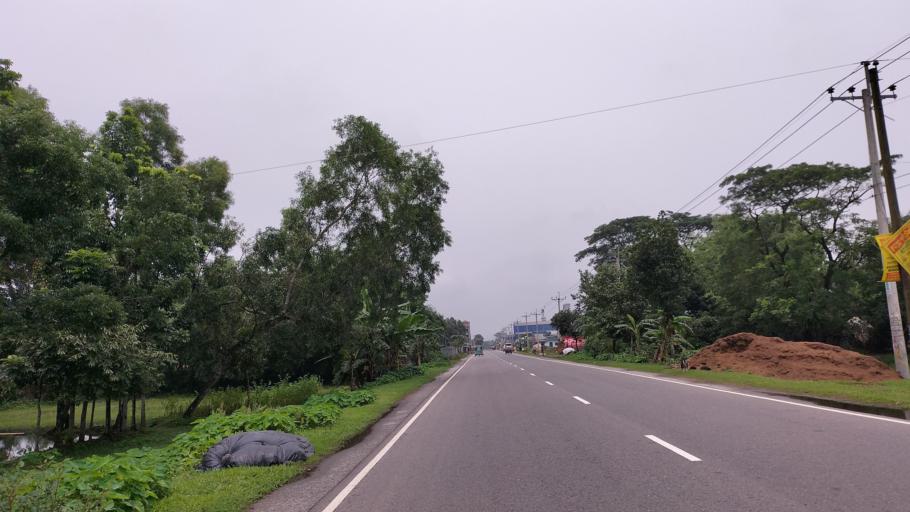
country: BD
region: Dhaka
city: Netrakona
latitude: 24.8512
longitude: 90.6243
